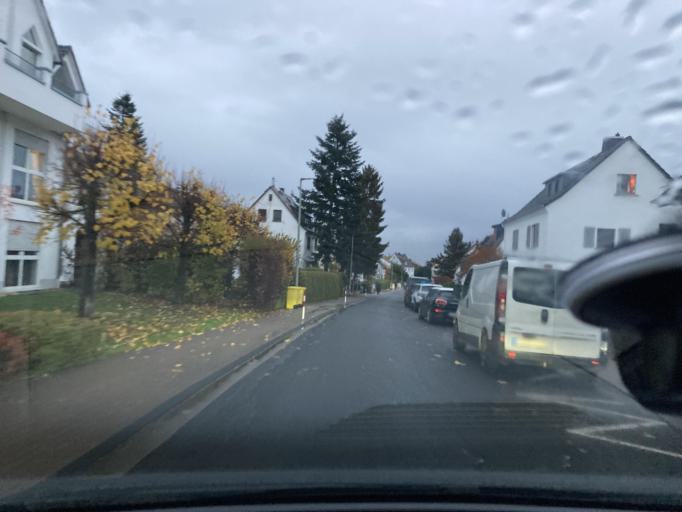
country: DE
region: Hesse
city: Kelkheim (Taunus)
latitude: 50.1314
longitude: 8.4470
